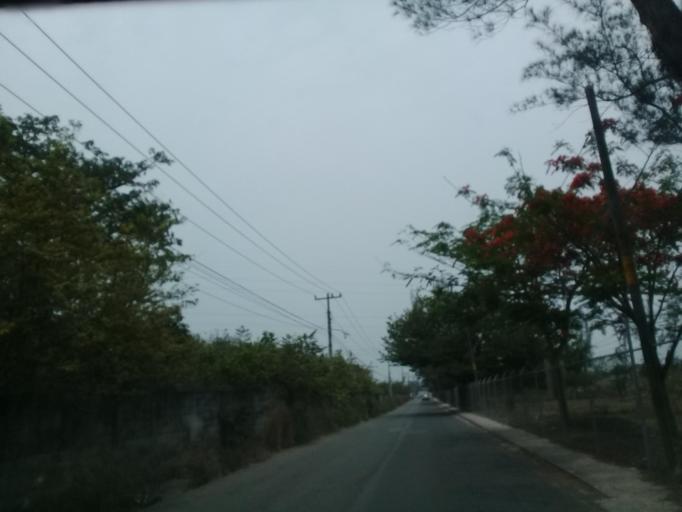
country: MX
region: Veracruz
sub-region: Veracruz
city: Las Amapolas
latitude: 19.1577
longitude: -96.2090
